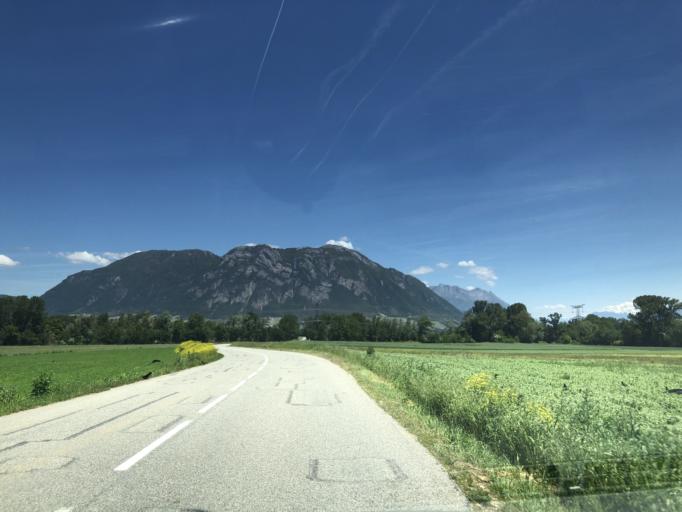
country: FR
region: Rhone-Alpes
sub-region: Departement de l'Isere
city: Chapareillan
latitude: 45.4703
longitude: 6.0055
